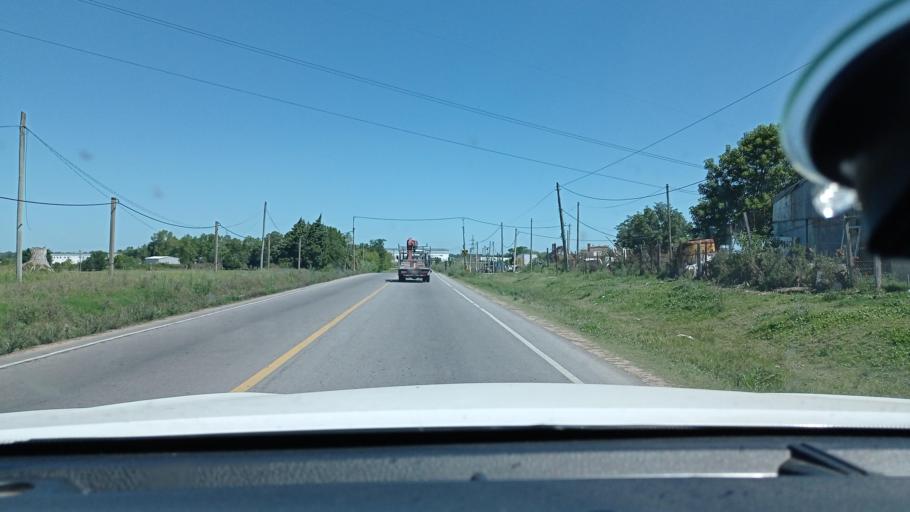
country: UY
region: Canelones
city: La Paz
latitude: -34.7809
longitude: -56.1675
